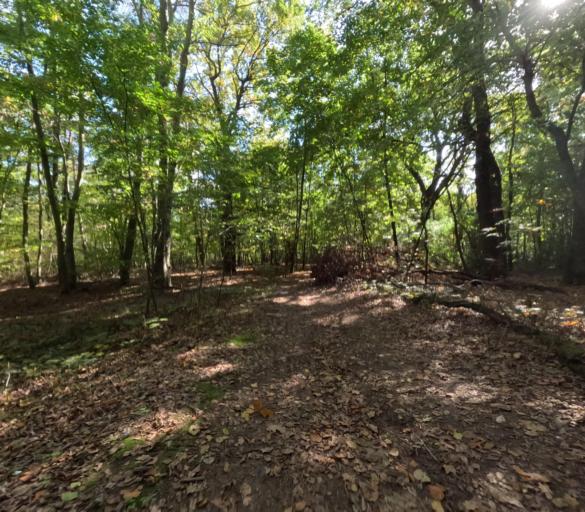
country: DE
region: Saxony
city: Albertstadt
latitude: 51.1061
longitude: 13.7428
